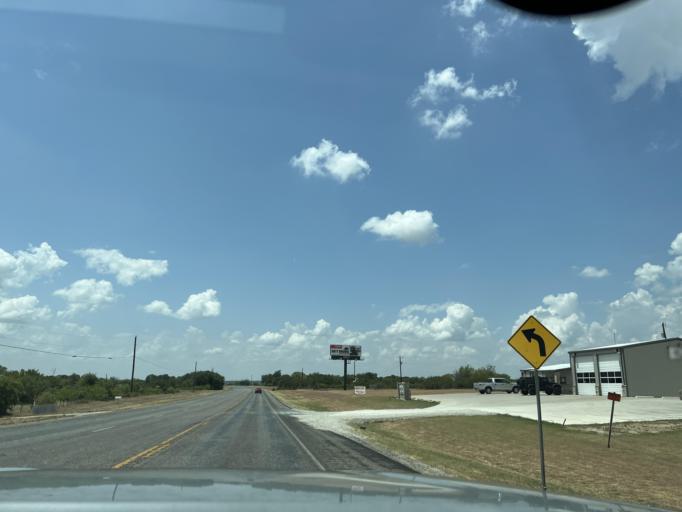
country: US
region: Texas
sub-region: Parker County
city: Springtown
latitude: 32.8983
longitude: -97.7286
